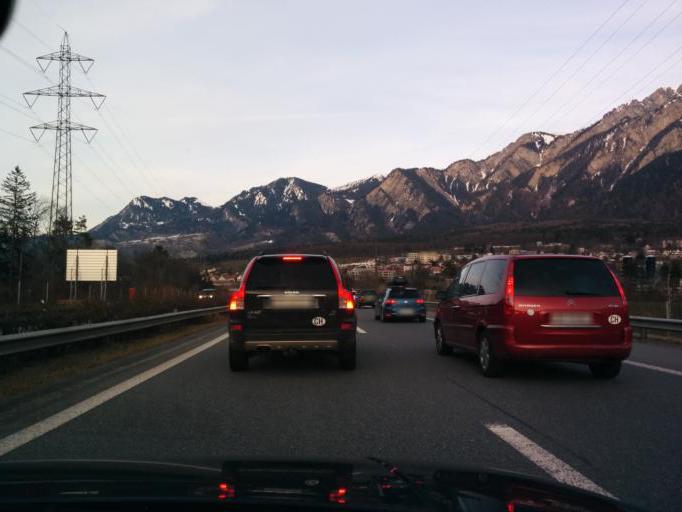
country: CH
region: Grisons
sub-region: Plessur District
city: Chur
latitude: 46.8697
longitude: 9.5253
